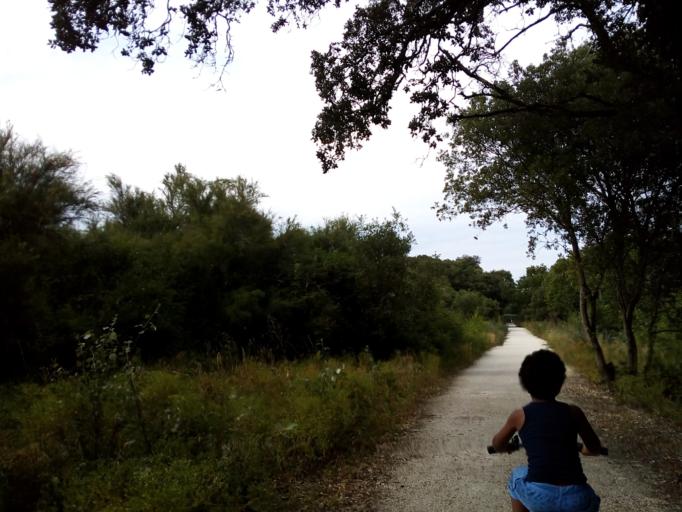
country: FR
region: Poitou-Charentes
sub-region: Departement de la Charente-Maritime
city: Boyard-Ville
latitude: 45.9560
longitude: -1.2450
